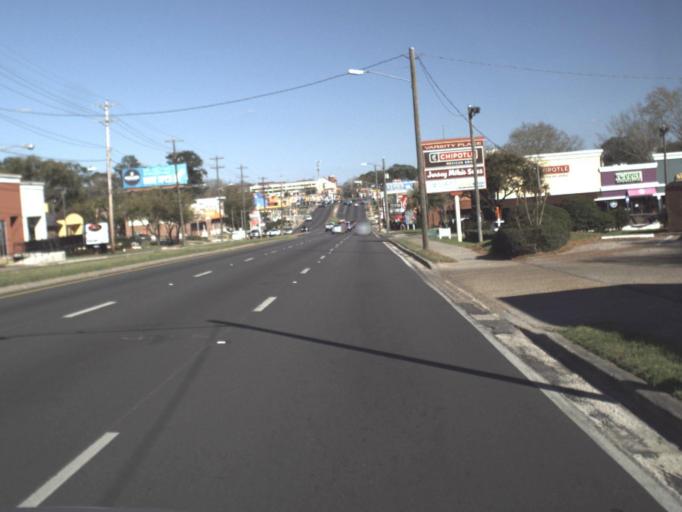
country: US
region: Florida
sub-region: Leon County
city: Tallahassee
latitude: 30.4490
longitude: -84.3123
